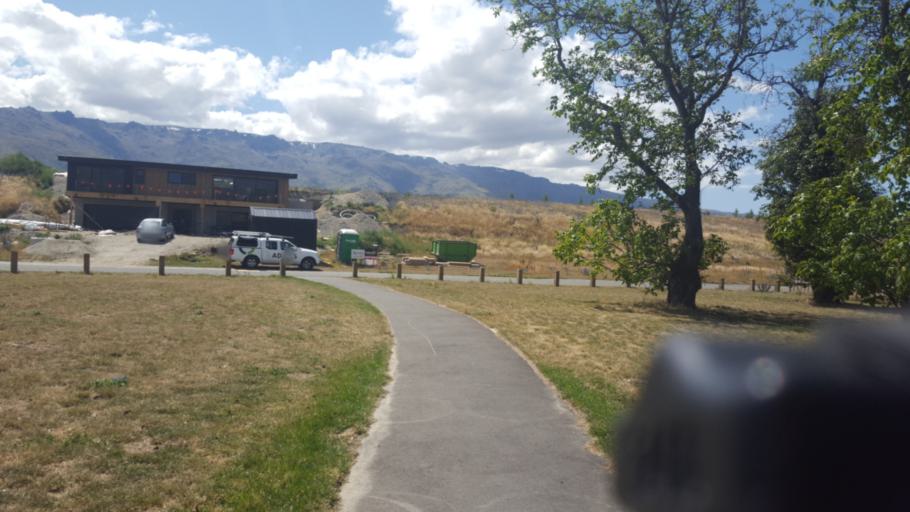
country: NZ
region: Otago
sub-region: Queenstown-Lakes District
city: Wanaka
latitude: -44.9750
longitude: 169.2408
